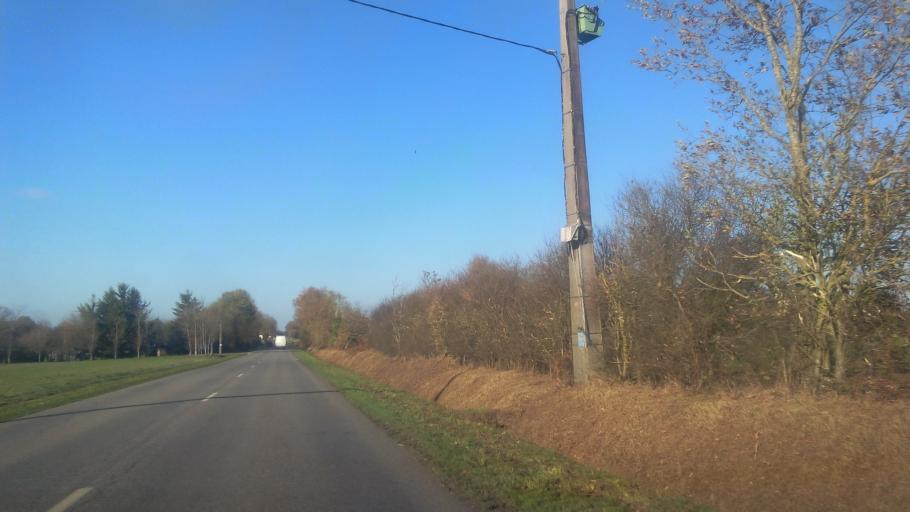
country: FR
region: Brittany
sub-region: Departement du Morbihan
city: Saint-Vincent-sur-Oust
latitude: 47.7091
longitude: -2.1681
